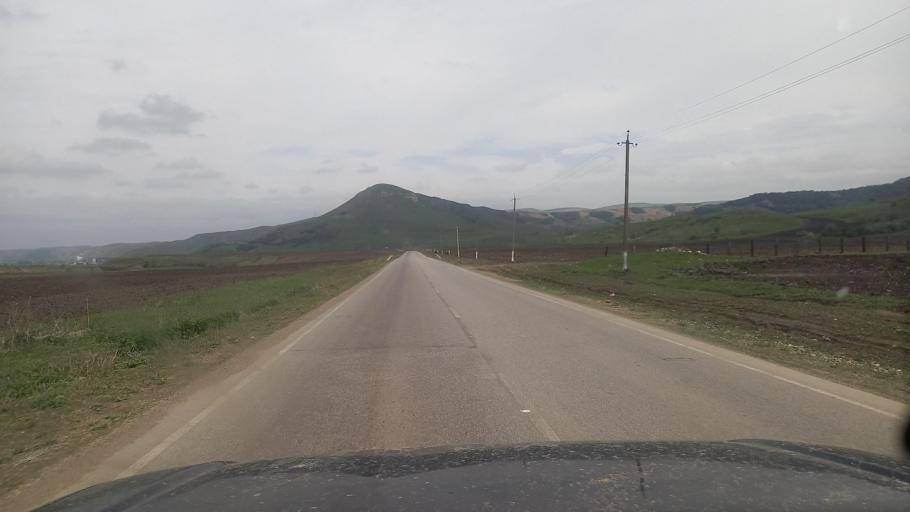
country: RU
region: Kabardino-Balkariya
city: Kamennomostskoye
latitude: 43.7268
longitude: 43.1124
